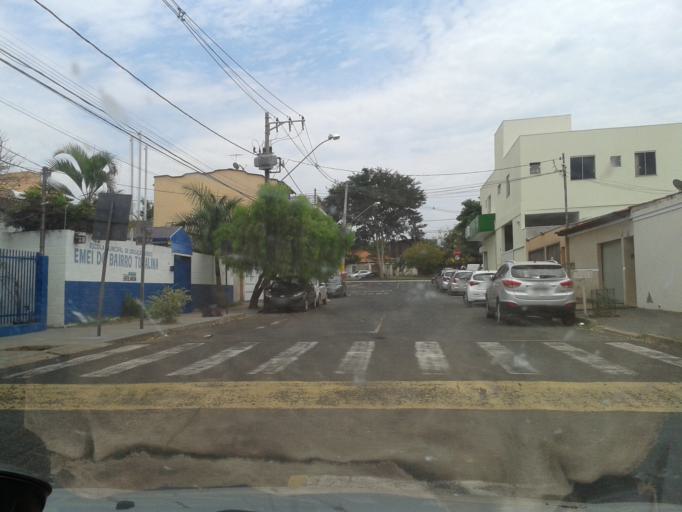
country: BR
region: Minas Gerais
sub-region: Uberlandia
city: Uberlandia
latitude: -18.9349
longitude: -48.3035
